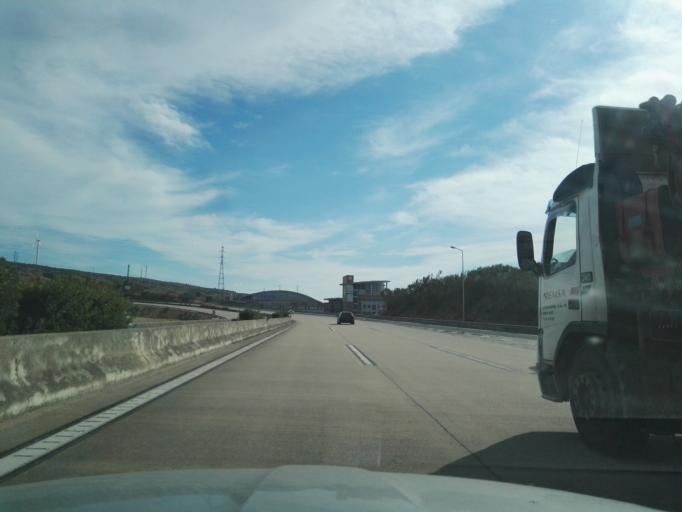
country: PT
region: Lisbon
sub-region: Loures
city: Santo Antao do Tojal
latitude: 38.8682
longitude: -9.1397
